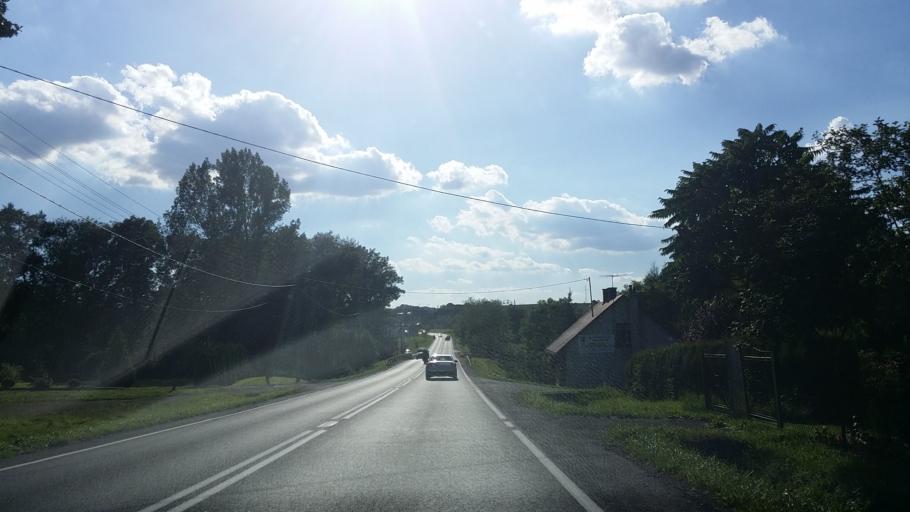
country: PL
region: Lesser Poland Voivodeship
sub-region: Powiat wadowicki
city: Inwald
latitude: 49.8684
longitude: 19.4185
